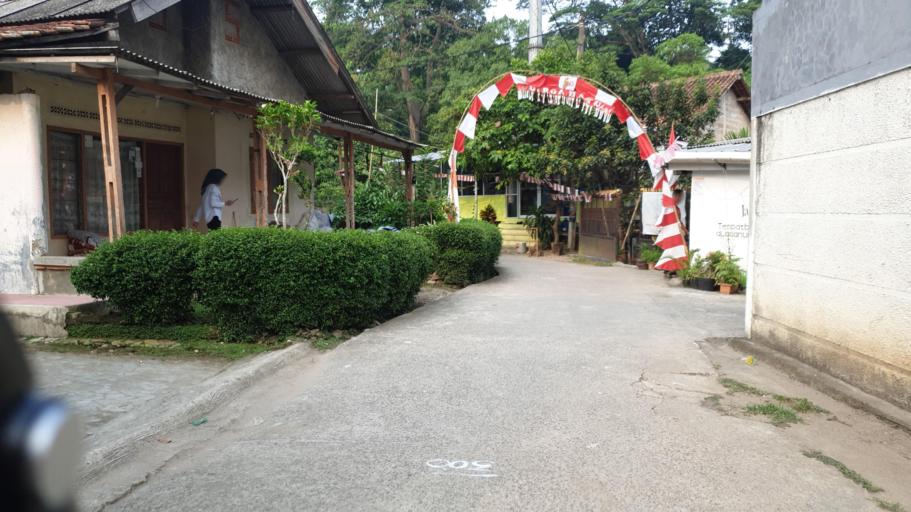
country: ID
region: West Java
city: Depok
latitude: -6.3682
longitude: 106.8407
